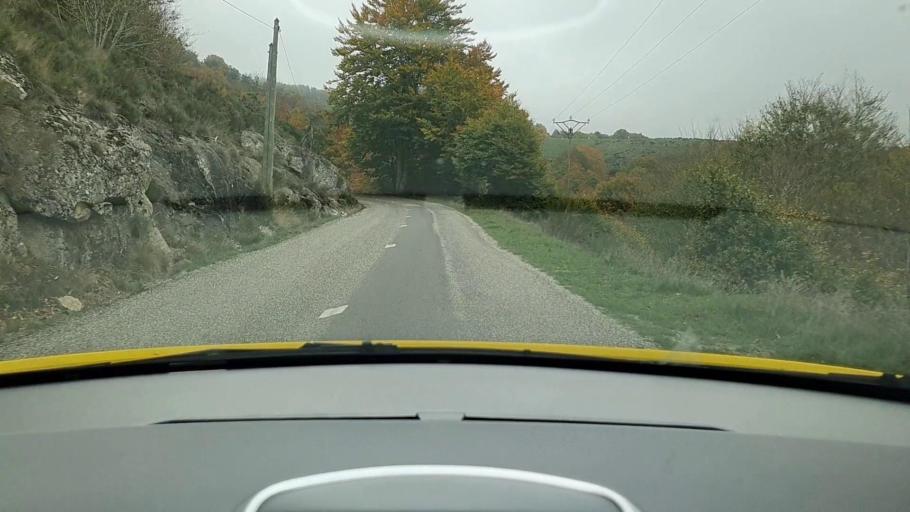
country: FR
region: Languedoc-Roussillon
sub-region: Departement du Gard
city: Le Vigan
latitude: 44.0757
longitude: 3.5122
